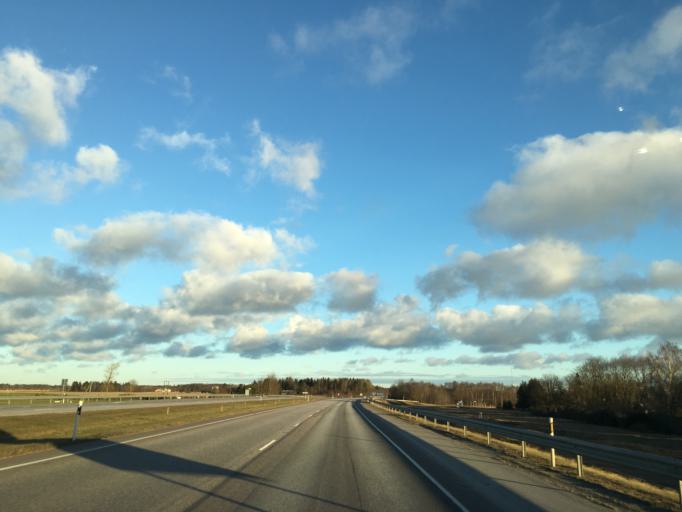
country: EE
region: Harju
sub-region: Saue linn
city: Saue
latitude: 59.2749
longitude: 24.5228
